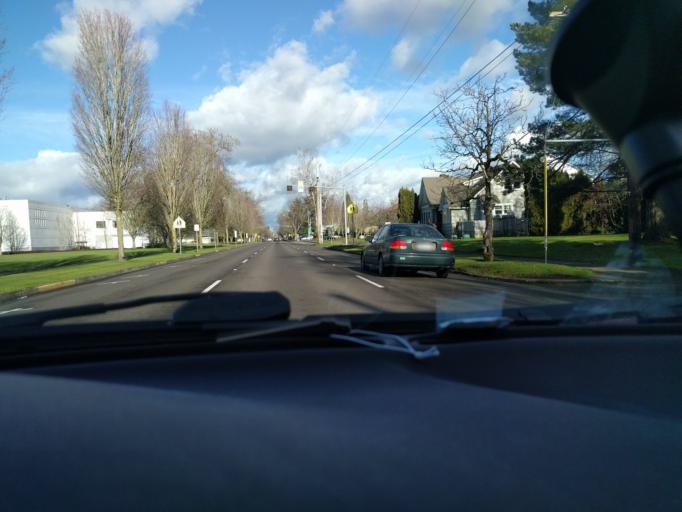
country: US
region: Oregon
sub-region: Marion County
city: Salem
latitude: 44.9445
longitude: -123.0256
